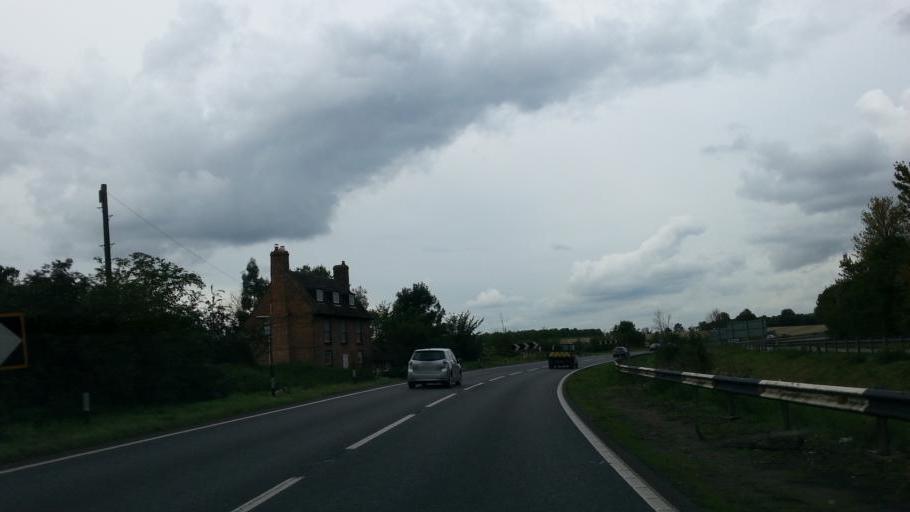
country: GB
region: England
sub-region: Cambridgeshire
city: Little Paxton
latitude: 52.2674
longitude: -0.2624
